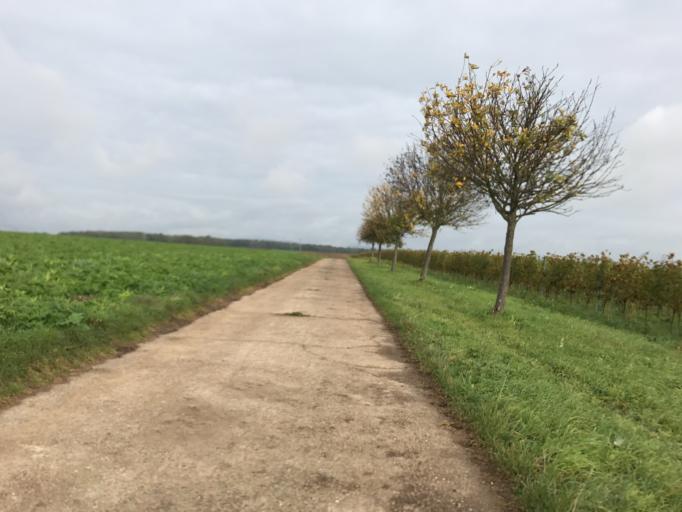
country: DE
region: Rheinland-Pfalz
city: Bubenheim
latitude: 49.9202
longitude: 8.0672
